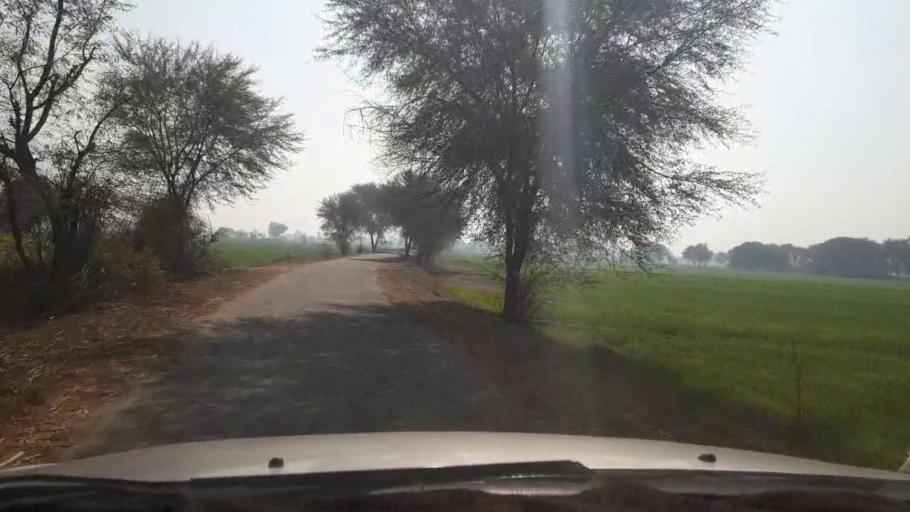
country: PK
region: Sindh
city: Khanpur
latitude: 27.7437
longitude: 69.5043
